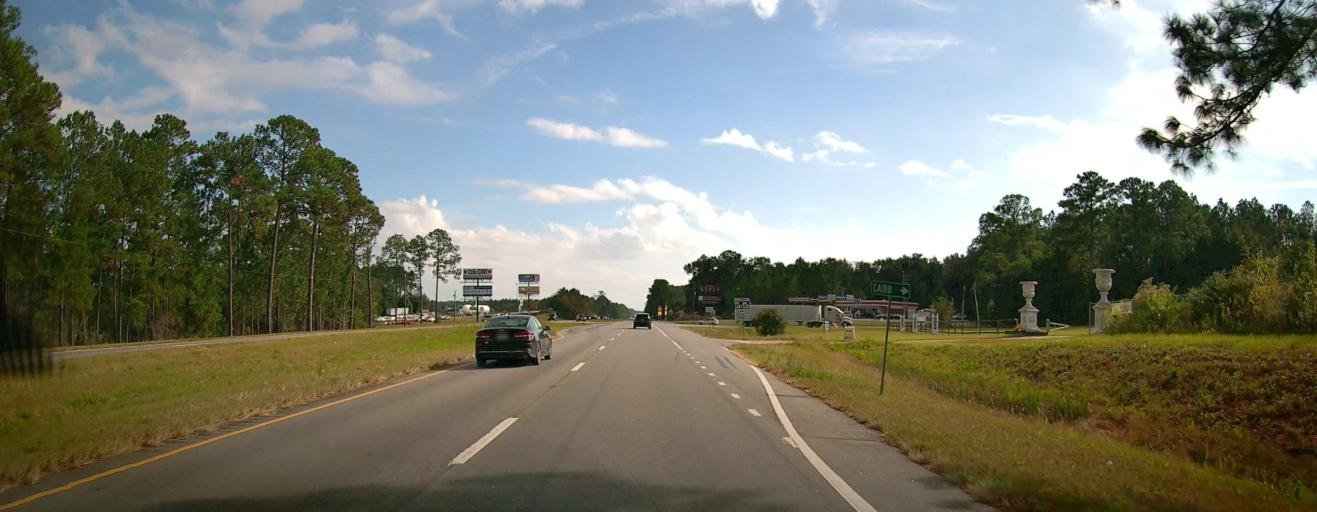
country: US
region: Georgia
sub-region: Thomas County
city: Meigs
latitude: 30.9787
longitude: -84.0380
